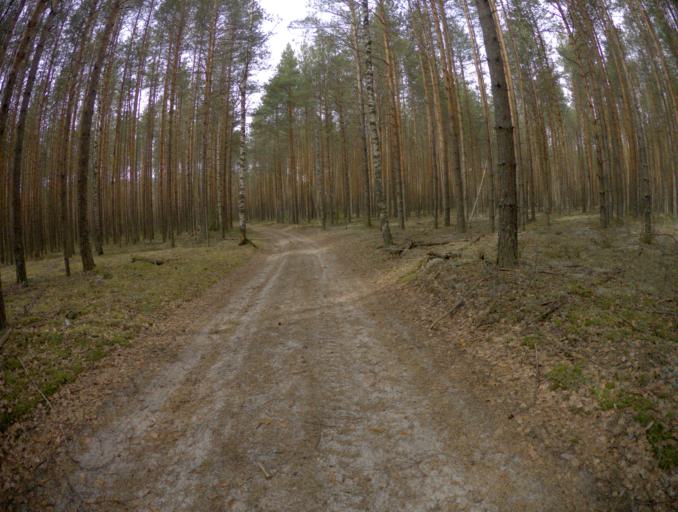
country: RU
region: Vladimir
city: Raduzhnyy
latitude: 55.9473
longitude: 40.2722
